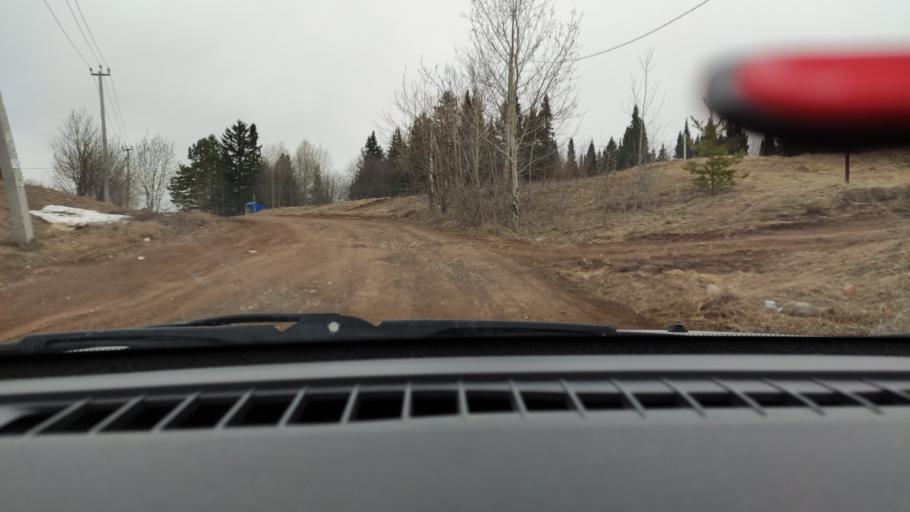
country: RU
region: Perm
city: Kultayevo
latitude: 57.8979
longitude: 56.0125
